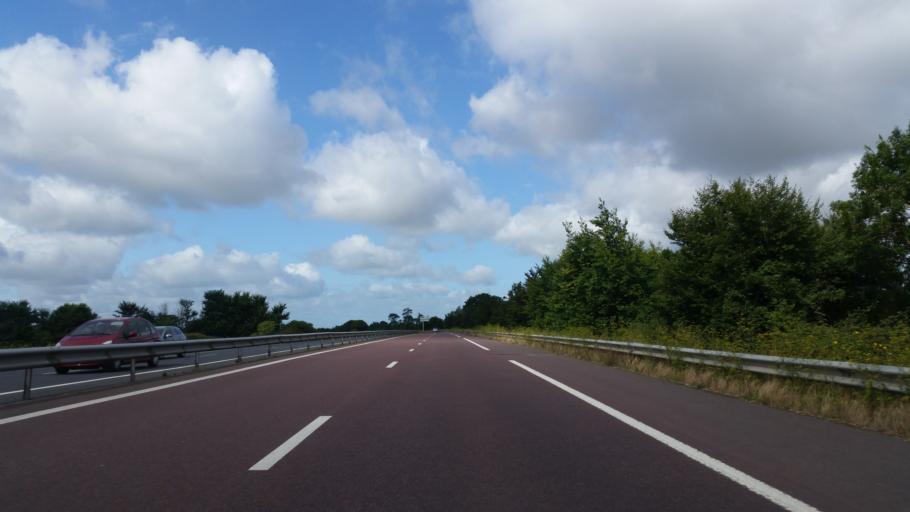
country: FR
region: Lower Normandy
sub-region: Departement du Calvados
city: Grandcamp-Maisy
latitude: 49.3425
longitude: -1.0460
